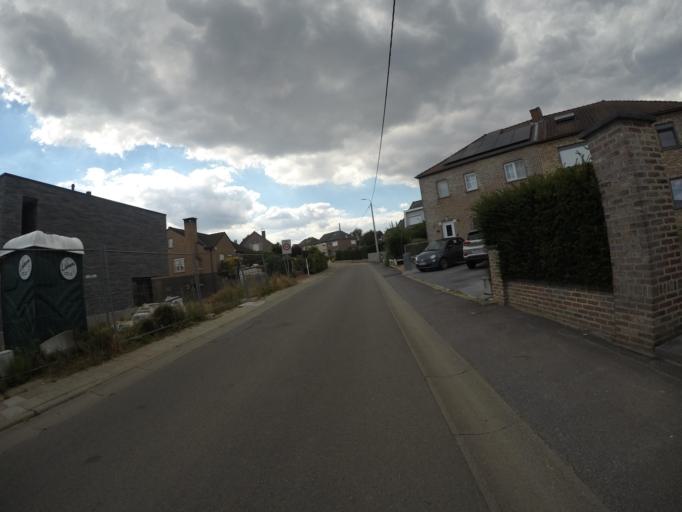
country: BE
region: Flanders
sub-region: Provincie Vlaams-Brabant
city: Ledeberg
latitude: 50.8491
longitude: 4.1049
